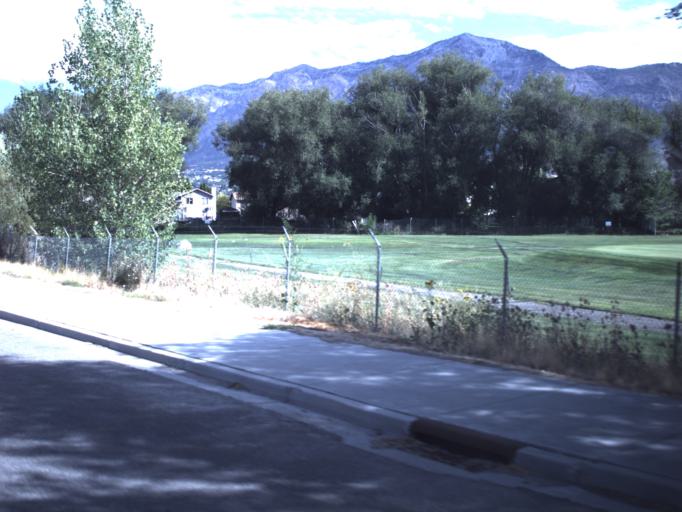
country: US
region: Utah
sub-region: Weber County
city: Harrisville
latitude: 41.2931
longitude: -111.9935
